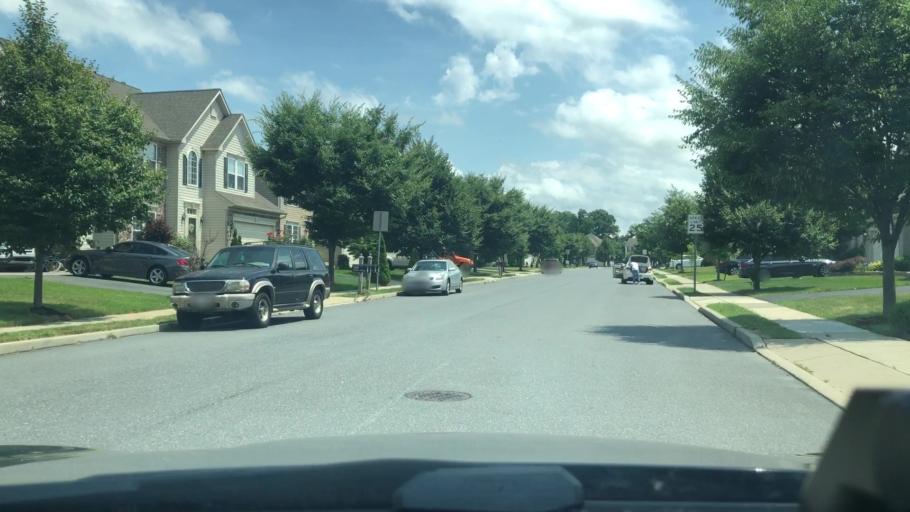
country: US
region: Pennsylvania
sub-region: Northampton County
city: Bethlehem
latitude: 40.6533
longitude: -75.4017
